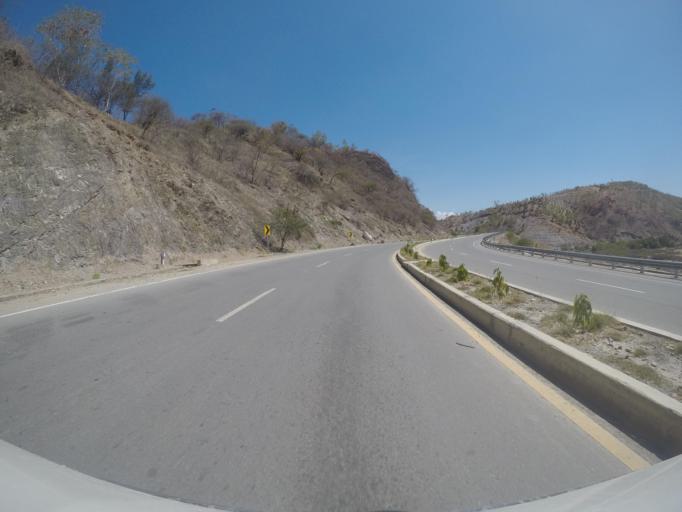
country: TL
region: Dili
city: Dili
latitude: -8.5585
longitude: 125.4959
